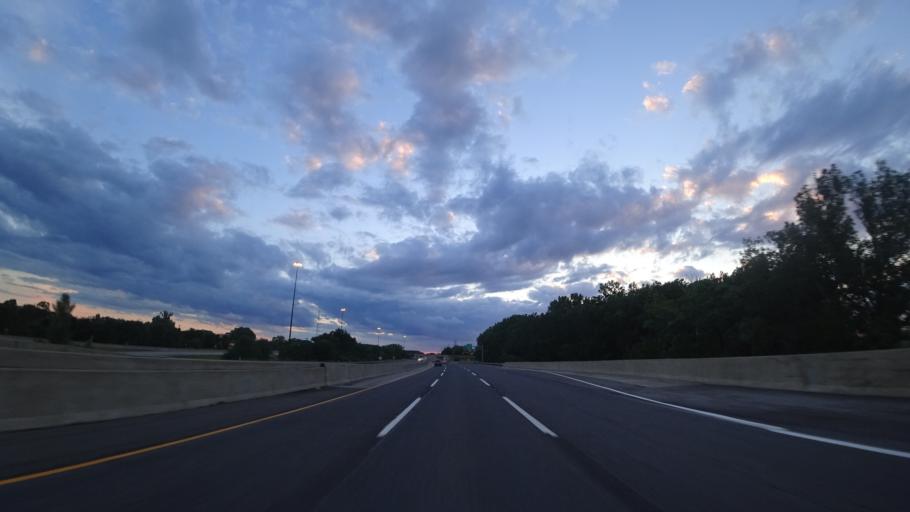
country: US
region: Indiana
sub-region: Lake County
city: Gary
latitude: 41.6089
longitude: -87.3525
